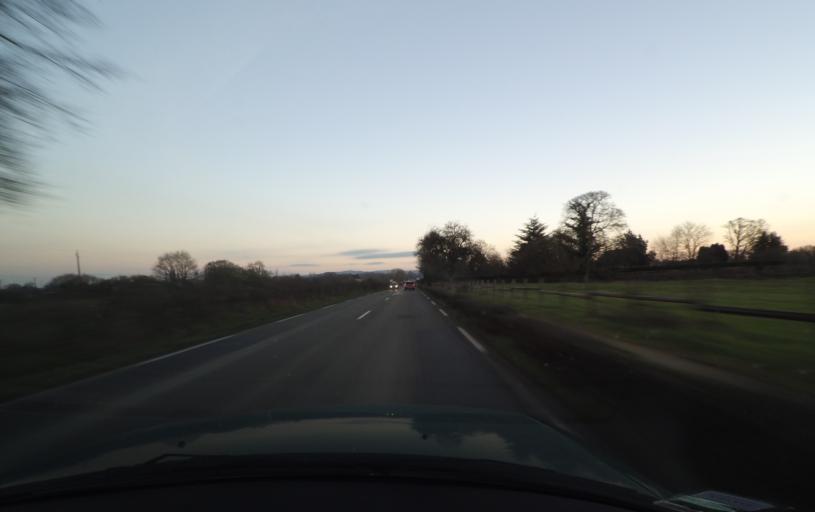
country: FR
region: Pays de la Loire
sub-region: Departement de la Mayenne
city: Evron
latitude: 48.1420
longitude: -0.4204
